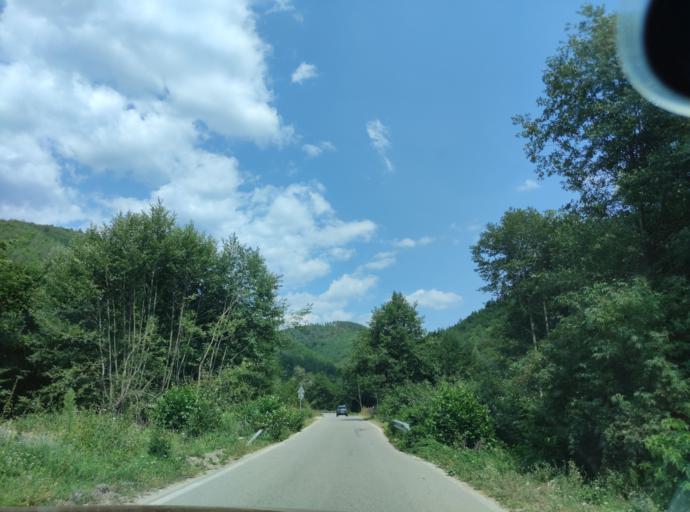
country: BG
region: Blagoevgrad
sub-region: Obshtina Belitsa
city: Belitsa
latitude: 42.0014
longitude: 23.5502
